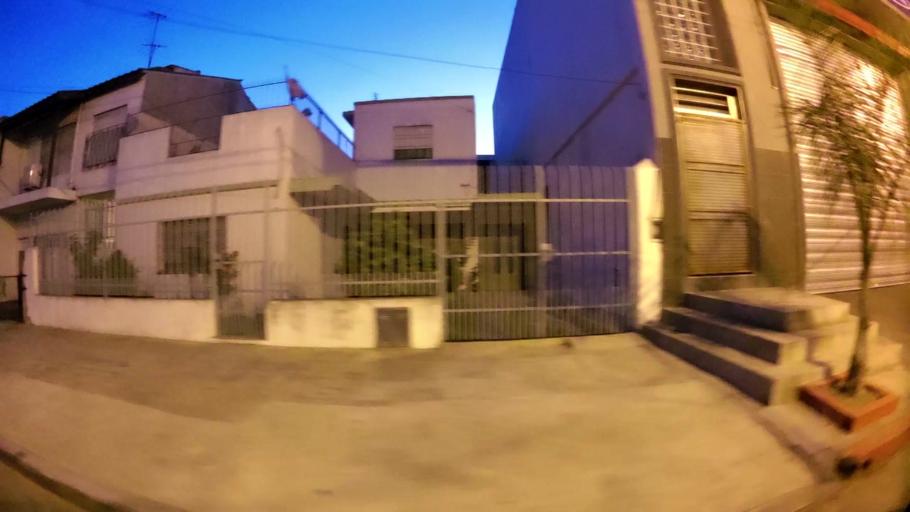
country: AR
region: Buenos Aires
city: San Justo
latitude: -34.7093
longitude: -58.5870
